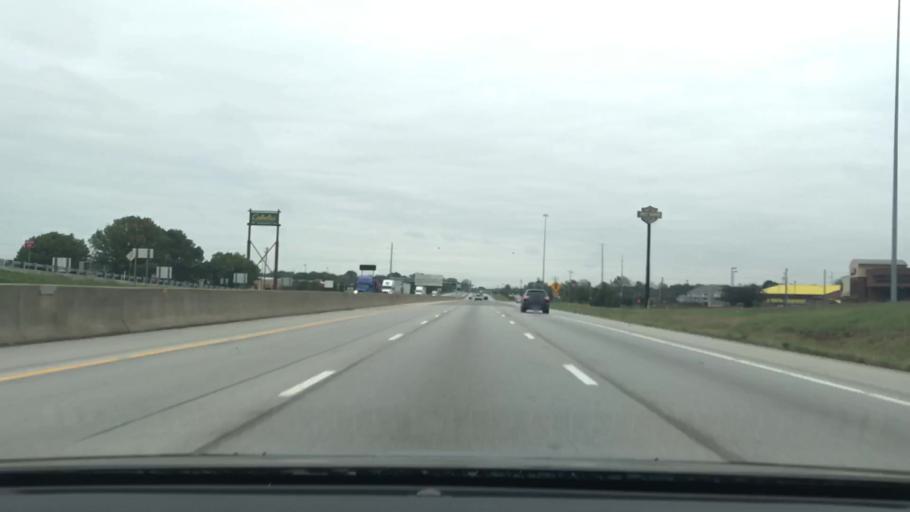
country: US
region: Kentucky
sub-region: Warren County
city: Plano
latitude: 36.9353
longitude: -86.4176
